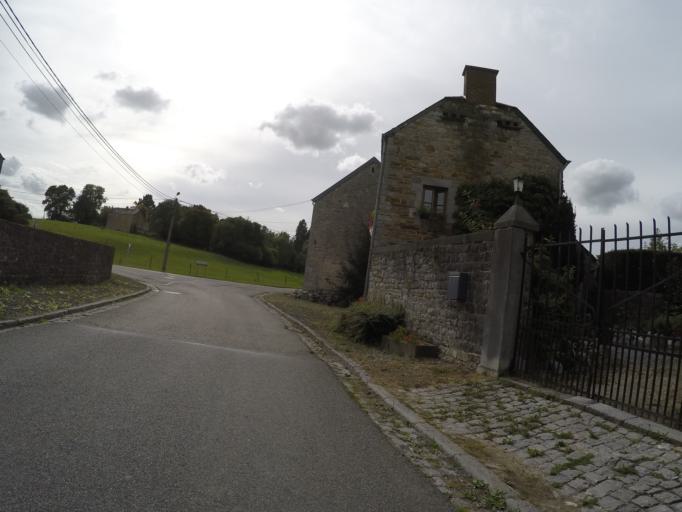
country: BE
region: Wallonia
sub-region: Province de Namur
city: Assesse
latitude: 50.3154
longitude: 4.9763
